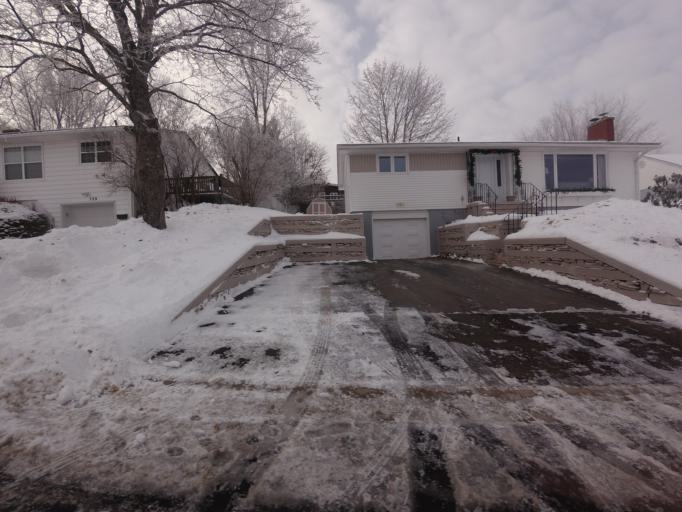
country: CA
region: New Brunswick
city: Oromocto
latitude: 45.8489
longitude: -66.4871
